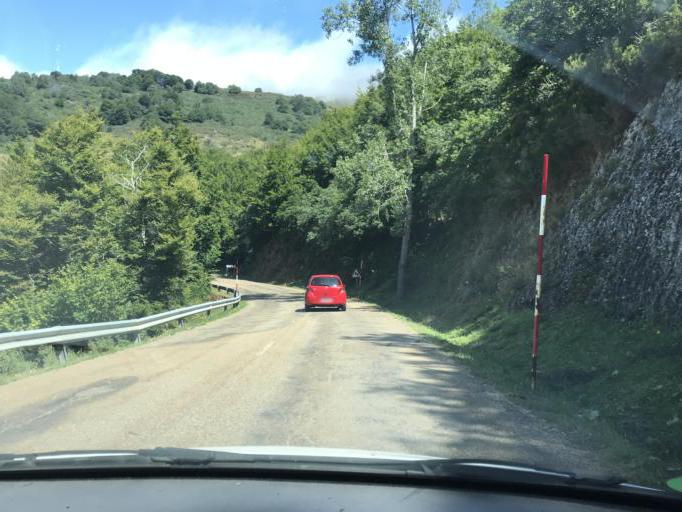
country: ES
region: Castille and Leon
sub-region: Provincia de Palencia
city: Polentinos
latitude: 43.0452
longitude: -4.4520
